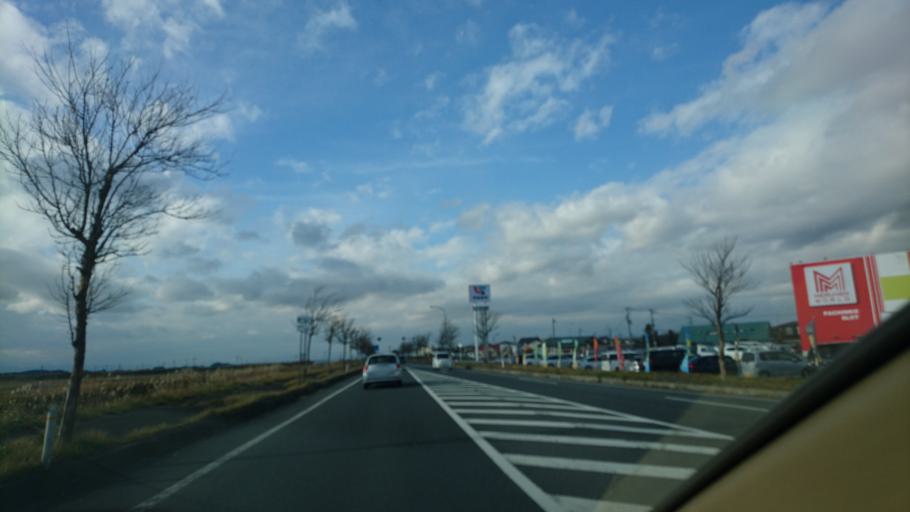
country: JP
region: Miyagi
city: Wakuya
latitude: 38.5316
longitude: 141.1277
